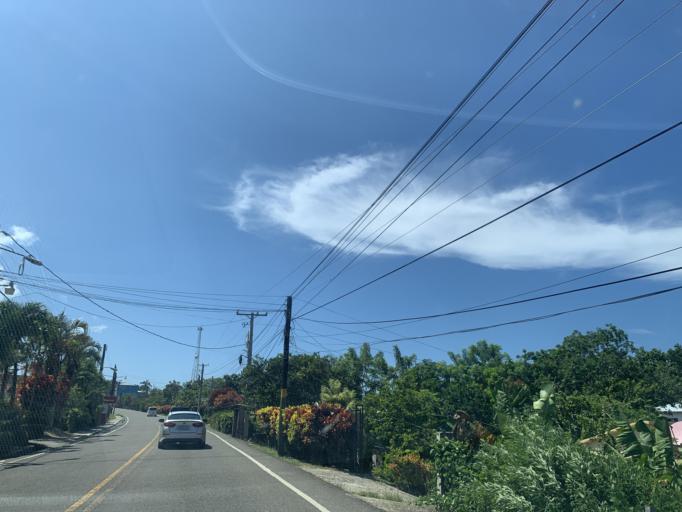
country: DO
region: Maria Trinidad Sanchez
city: Cabrera
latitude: 19.6705
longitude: -69.9547
